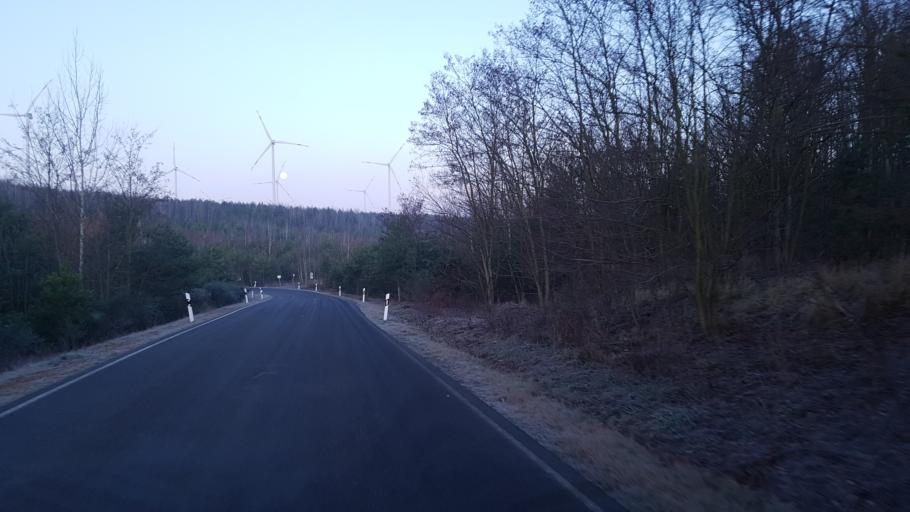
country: DE
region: Brandenburg
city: Schipkau
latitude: 51.5401
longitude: 13.8860
